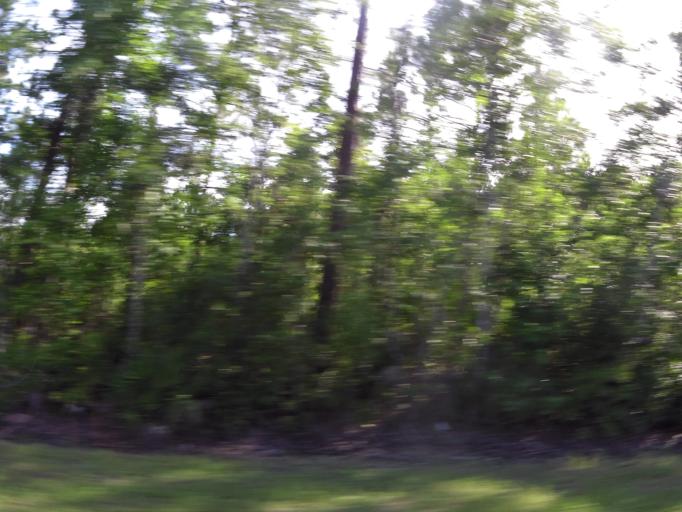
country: US
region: Florida
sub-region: Clay County
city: Green Cove Springs
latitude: 29.9961
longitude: -81.5395
